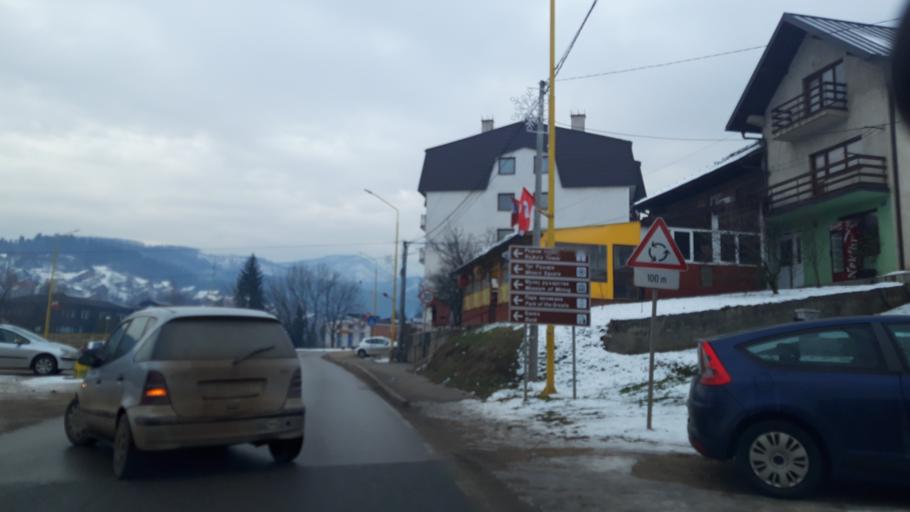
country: BA
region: Republika Srpska
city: Milici
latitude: 44.1707
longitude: 19.0766
